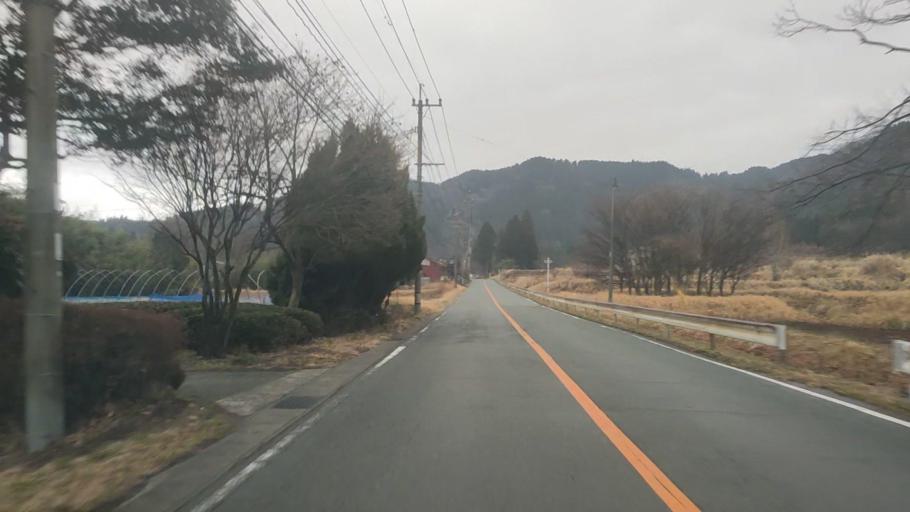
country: JP
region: Kumamoto
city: Aso
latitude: 32.8608
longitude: 131.1639
